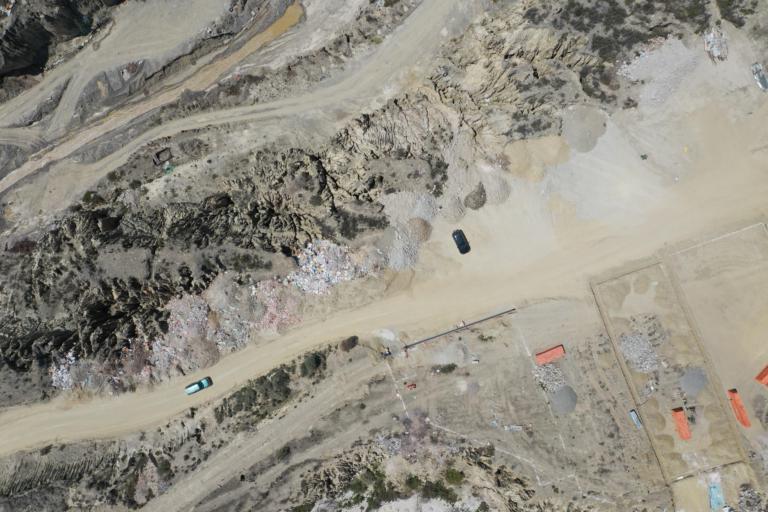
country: BO
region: La Paz
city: La Paz
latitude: -16.5638
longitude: -68.1154
